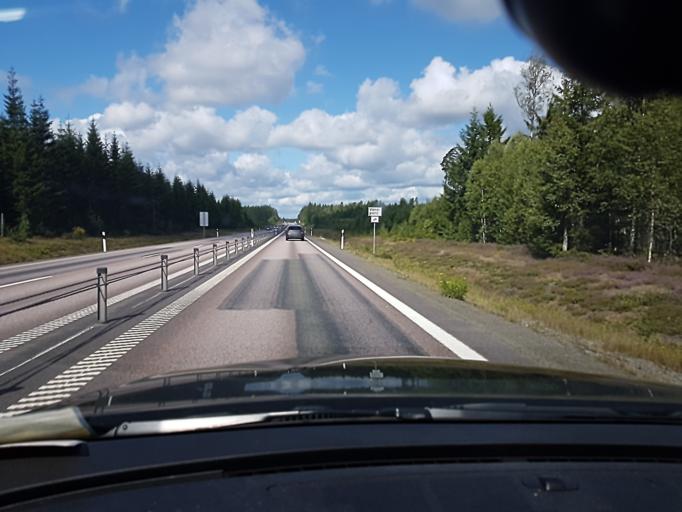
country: SE
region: Kalmar
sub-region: Emmaboda Kommun
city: Emmaboda
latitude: 56.7301
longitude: 15.5497
